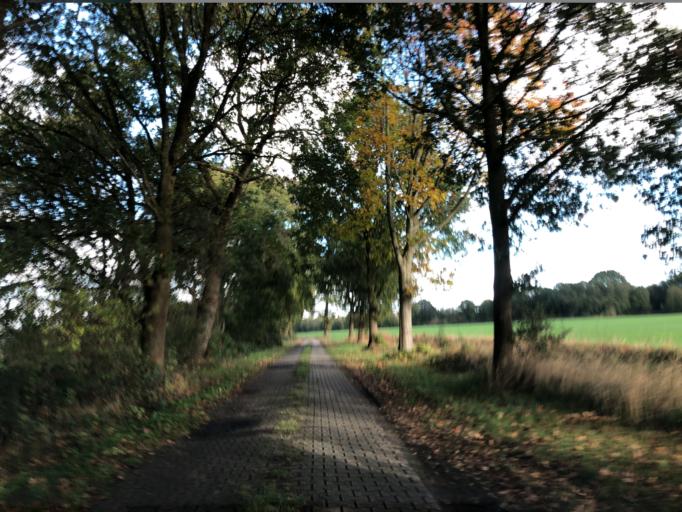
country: DE
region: Lower Saxony
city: Lehe
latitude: 53.0302
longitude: 7.3352
